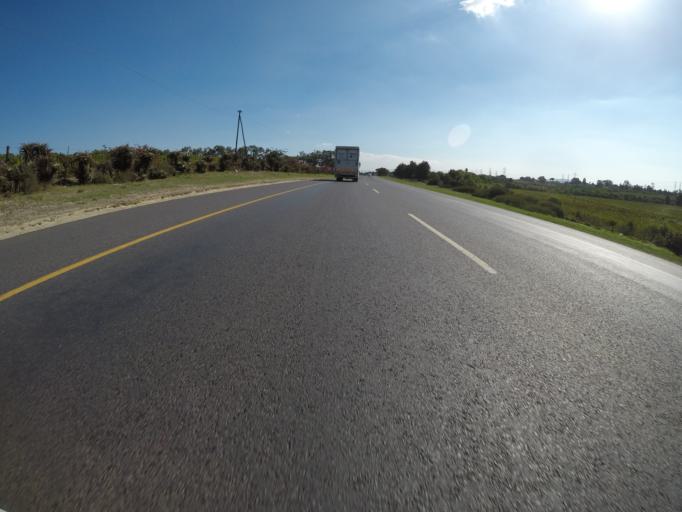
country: ZA
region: Western Cape
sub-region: City of Cape Town
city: Kraaifontein
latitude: -33.8994
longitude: 18.7302
